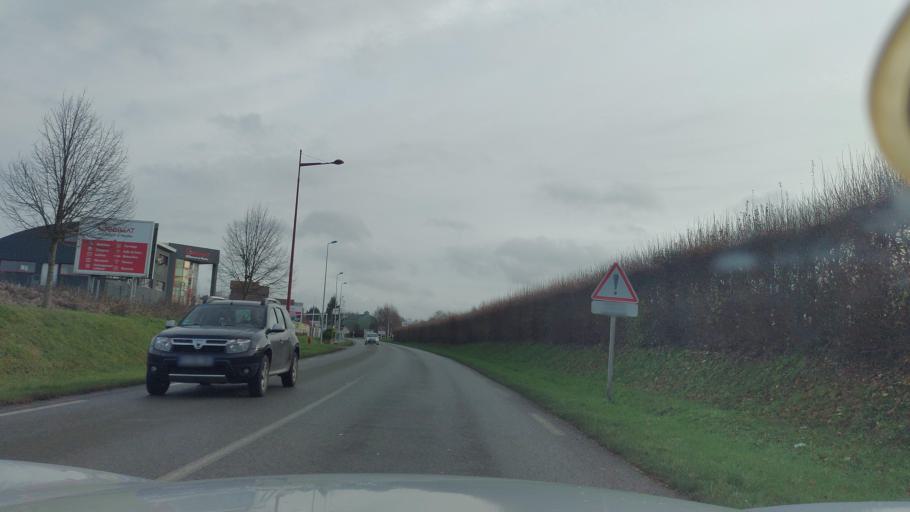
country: FR
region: Picardie
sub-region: Departement de la Somme
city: Oisemont
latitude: 49.9609
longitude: 1.7635
